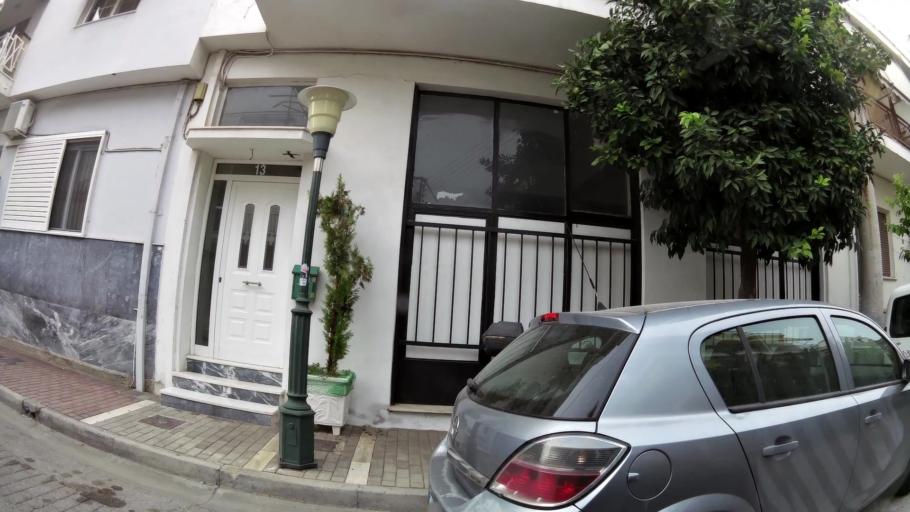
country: GR
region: Attica
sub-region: Nomarchia Athinas
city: Tavros
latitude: 37.9734
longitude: 23.6911
